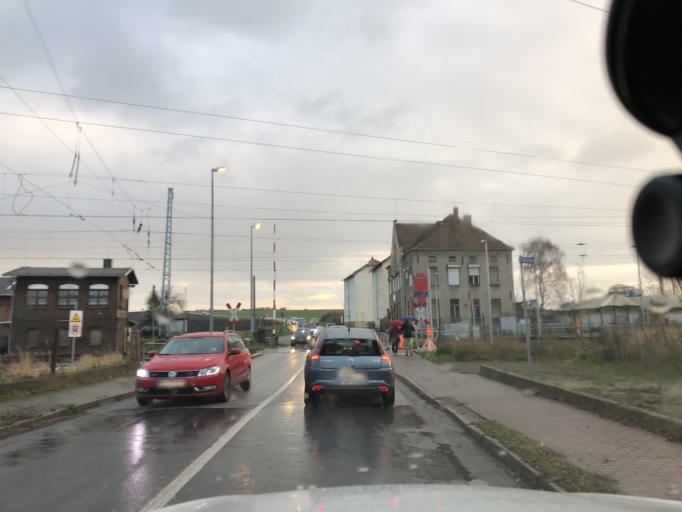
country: DE
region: Saxony-Anhalt
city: Langenbogen
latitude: 51.4649
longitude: 11.7837
